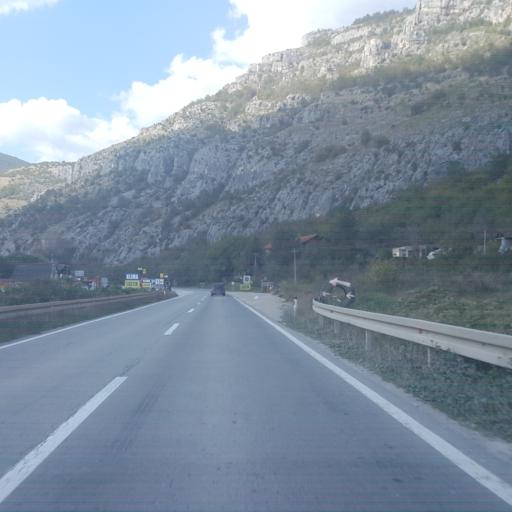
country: RS
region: Central Serbia
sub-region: Nisavski Okrug
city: Svrljig
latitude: 43.3085
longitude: 22.1867
